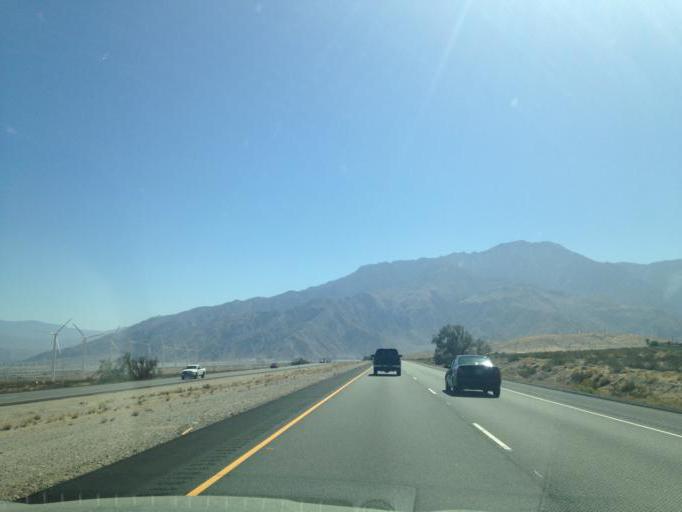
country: US
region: California
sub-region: Riverside County
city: Garnet
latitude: 33.9547
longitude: -116.5929
